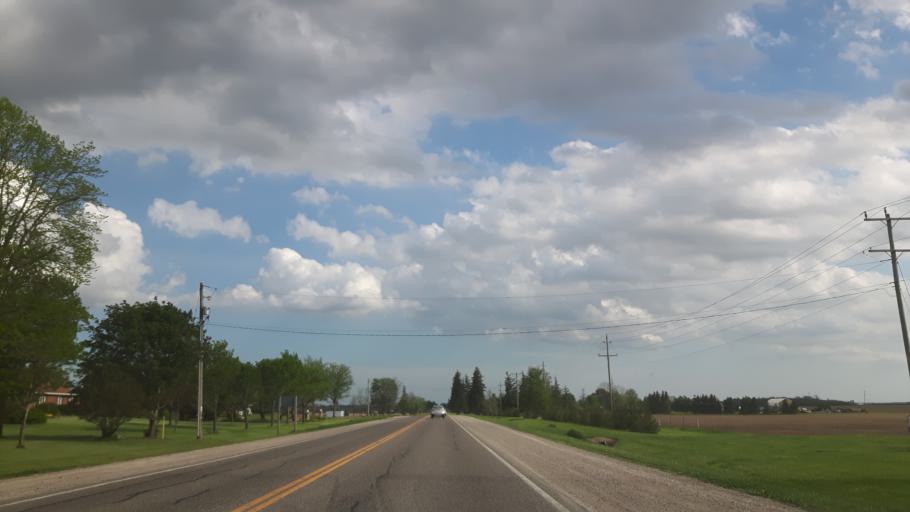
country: CA
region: Ontario
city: South Huron
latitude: 43.2341
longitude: -81.4581
